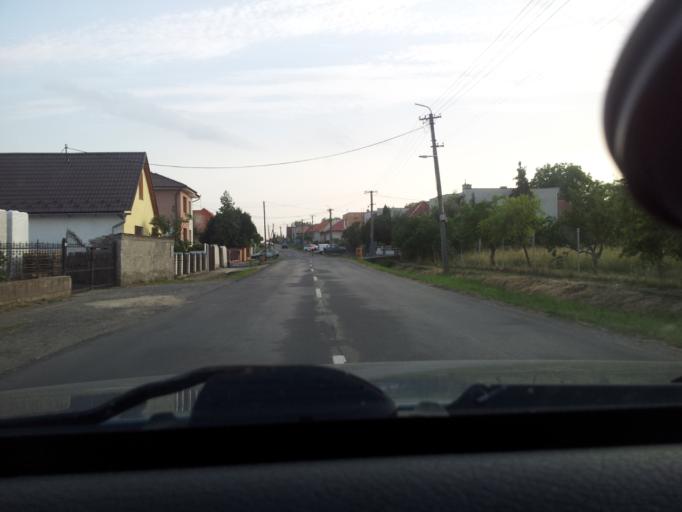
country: SK
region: Nitriansky
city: Levice
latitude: 48.2846
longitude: 18.6508
